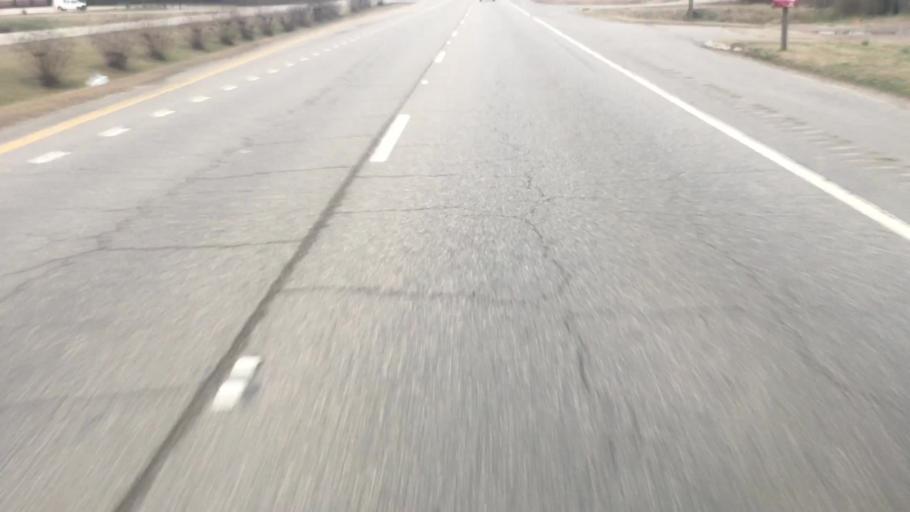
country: US
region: Alabama
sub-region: Walker County
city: Sumiton
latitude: 33.7411
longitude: -87.0371
